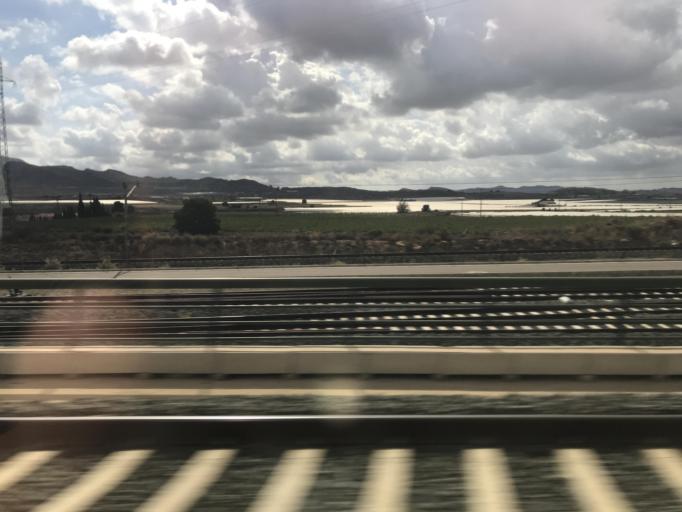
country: ES
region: Valencia
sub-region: Provincia de Alicante
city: Monforte del Cid
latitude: 38.4091
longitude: -0.6833
